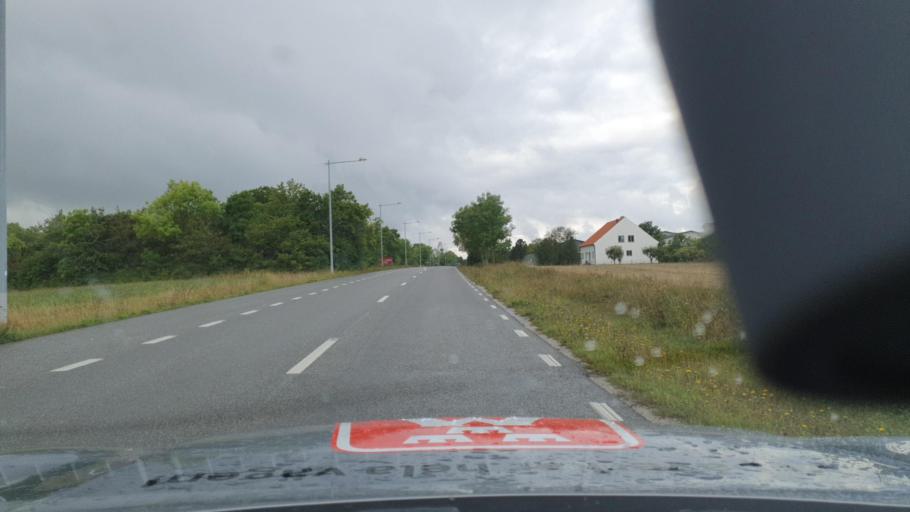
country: SE
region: Gotland
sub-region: Gotland
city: Slite
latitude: 57.8563
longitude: 19.0389
